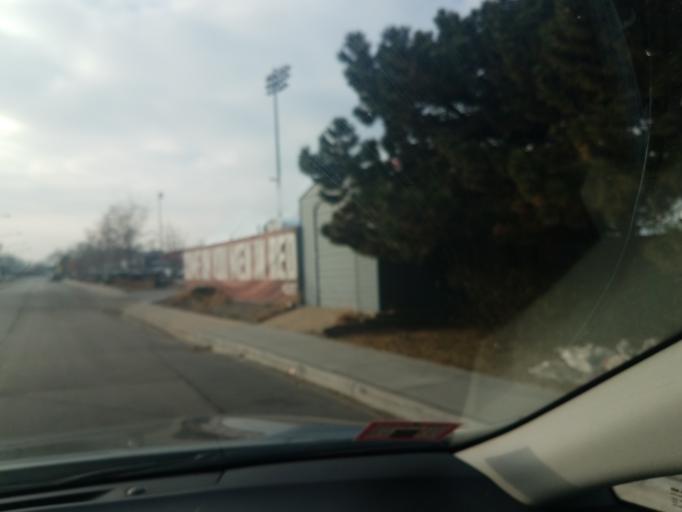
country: US
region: Illinois
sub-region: Cook County
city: Lincolnwood
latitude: 41.9491
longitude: -87.6949
